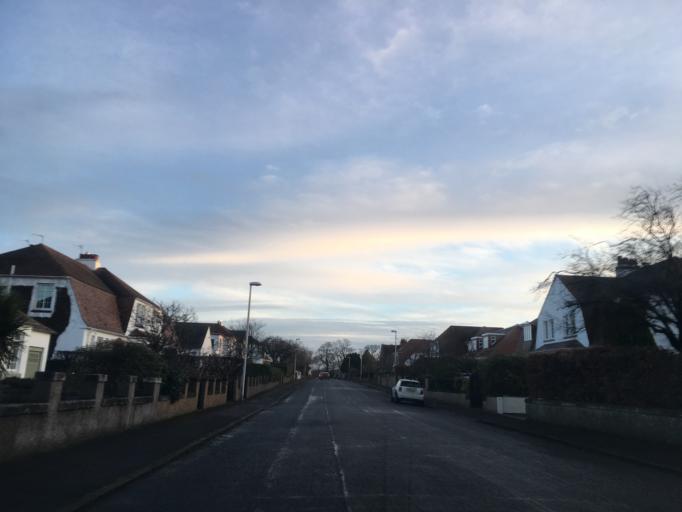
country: GB
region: Scotland
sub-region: Edinburgh
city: Colinton
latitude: 55.9502
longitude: -3.2464
